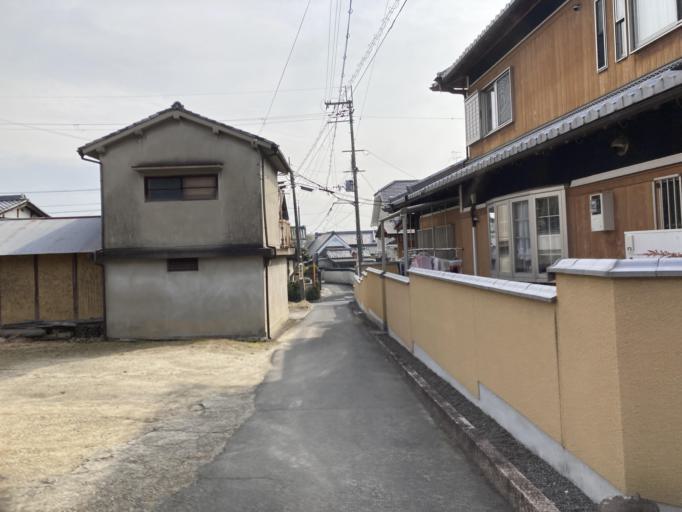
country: JP
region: Nara
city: Nara-shi
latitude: 34.6970
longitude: 135.7889
